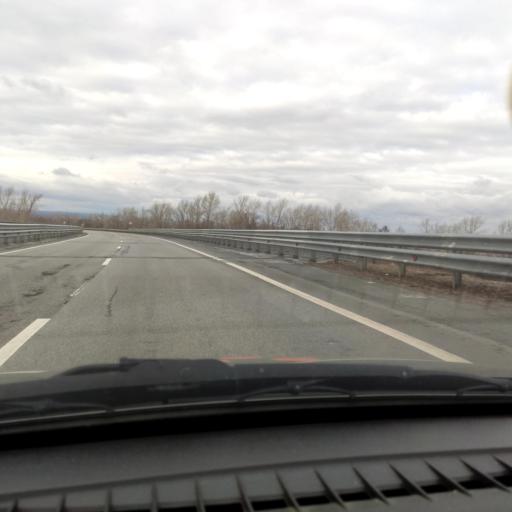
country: RU
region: Samara
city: Novosemeykino
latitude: 53.4160
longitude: 50.3389
